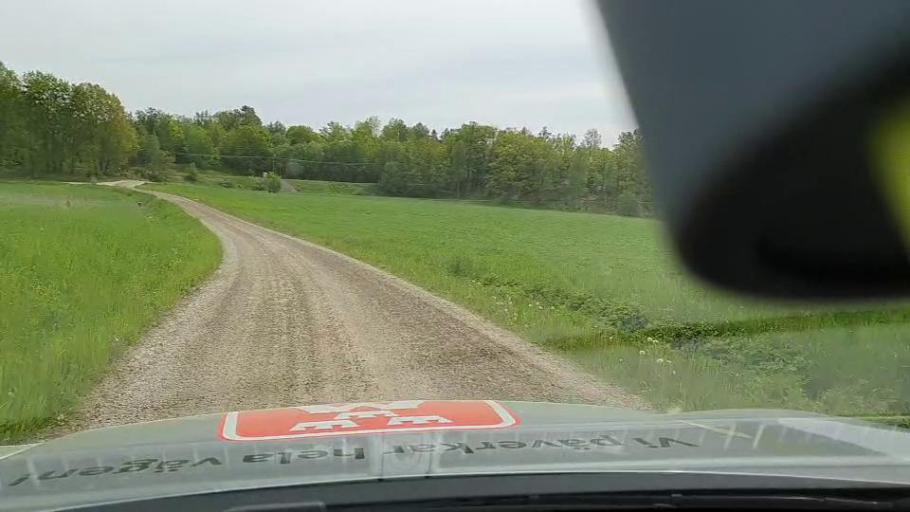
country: SE
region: Soedermanland
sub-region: Flens Kommun
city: Flen
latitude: 59.0414
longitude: 16.5779
